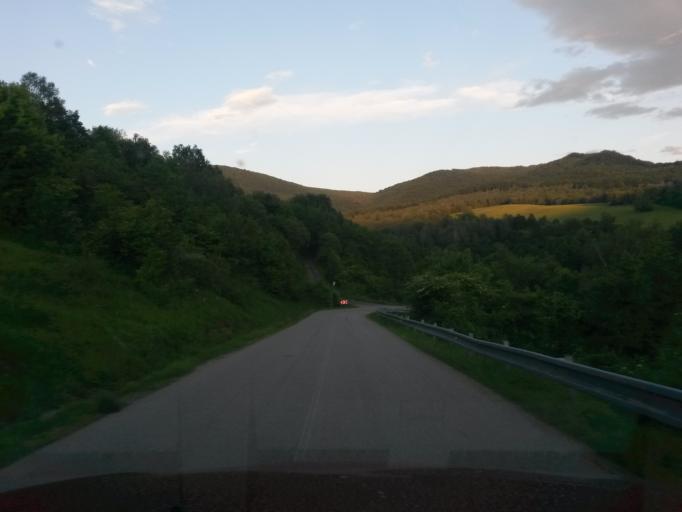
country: UA
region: Zakarpattia
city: Kamianytsia
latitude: 48.8158
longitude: 22.3452
